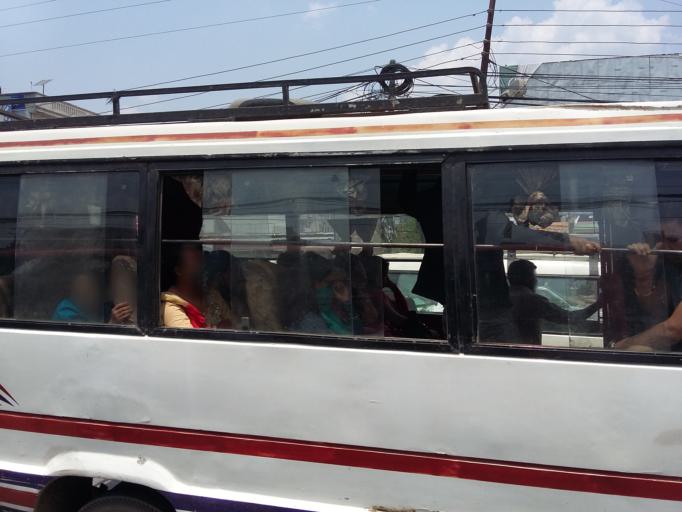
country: NP
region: Central Region
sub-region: Bagmati Zone
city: Kathmandu
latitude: 27.7352
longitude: 85.3182
